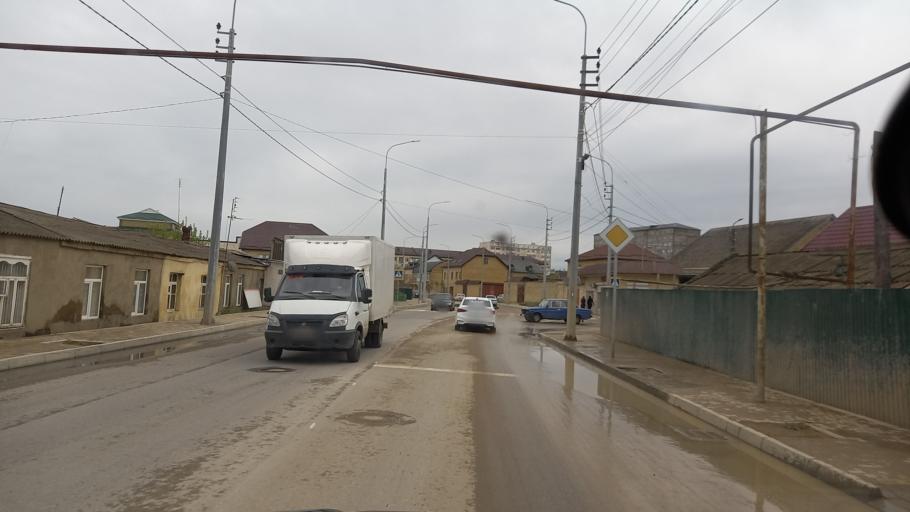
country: RU
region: Dagestan
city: Derbent
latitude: 42.0918
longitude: 48.2888
